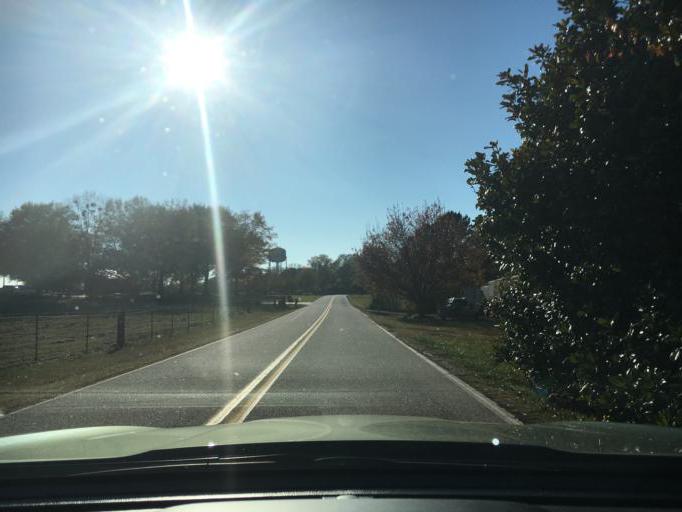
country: US
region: South Carolina
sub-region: Spartanburg County
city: Inman Mills
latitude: 35.0549
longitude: -82.1238
